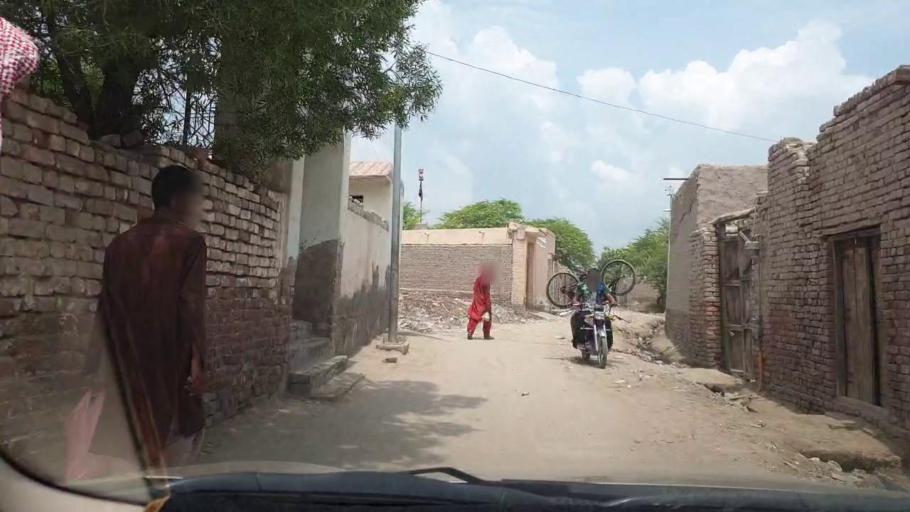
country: PK
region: Sindh
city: Larkana
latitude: 27.5611
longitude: 68.1234
